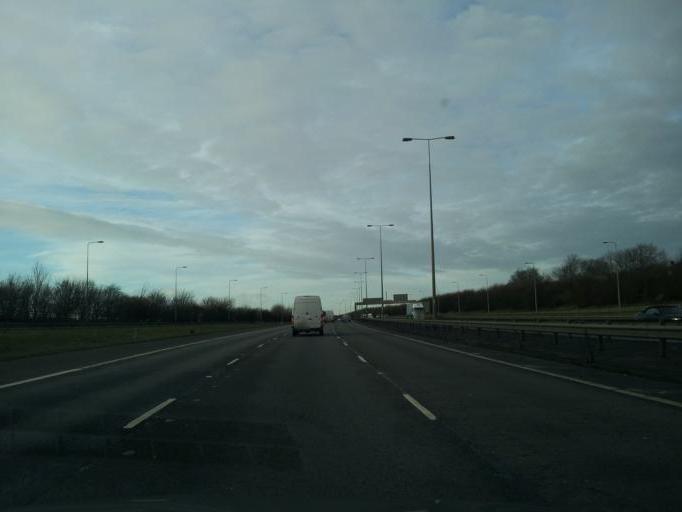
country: GB
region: England
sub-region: Cambridgeshire
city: Stilton
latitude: 52.5045
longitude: -0.2943
